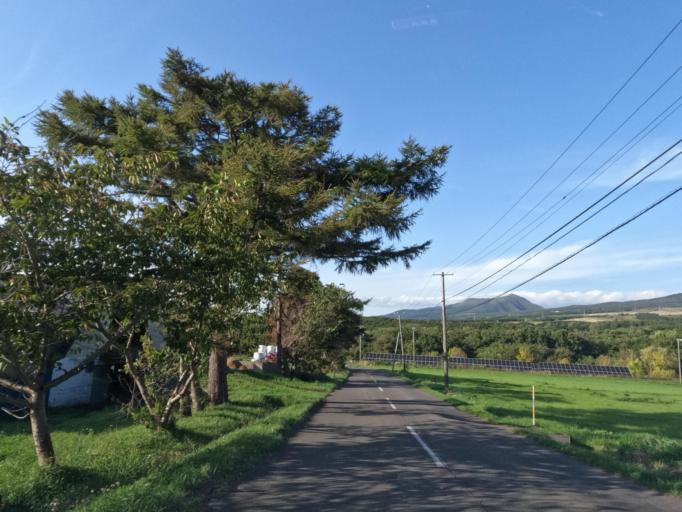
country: JP
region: Hokkaido
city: Muroran
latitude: 42.3964
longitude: 140.9346
